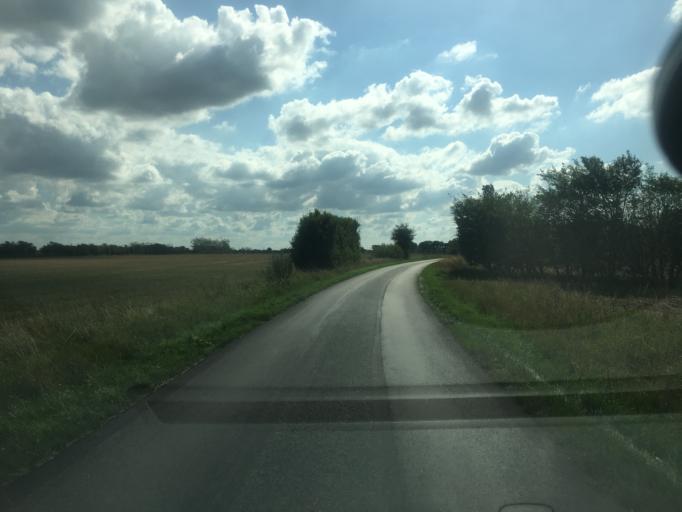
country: DK
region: South Denmark
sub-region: Tonder Kommune
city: Logumkloster
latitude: 54.9848
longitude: 8.9966
